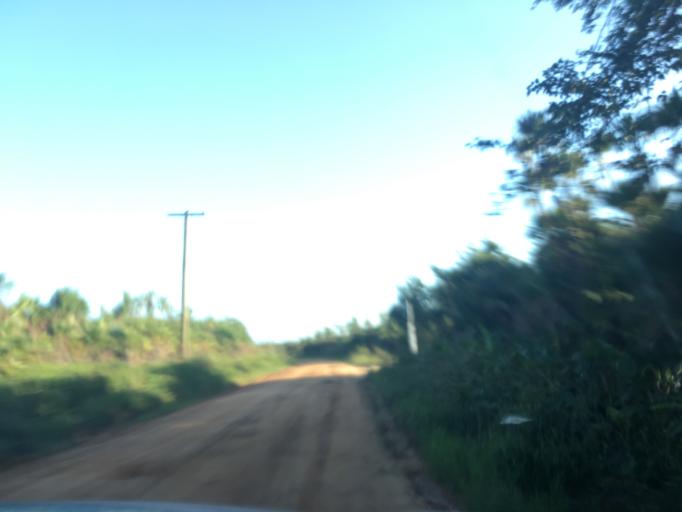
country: BZ
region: Stann Creek
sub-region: Dangriga
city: Dangriga
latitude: 16.8302
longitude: -88.2745
